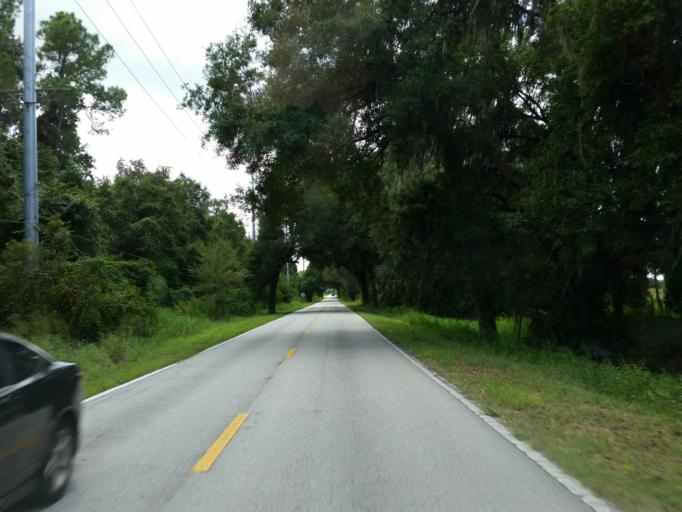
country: US
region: Florida
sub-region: Hillsborough County
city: Pebble Creek
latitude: 28.1647
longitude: -82.2658
